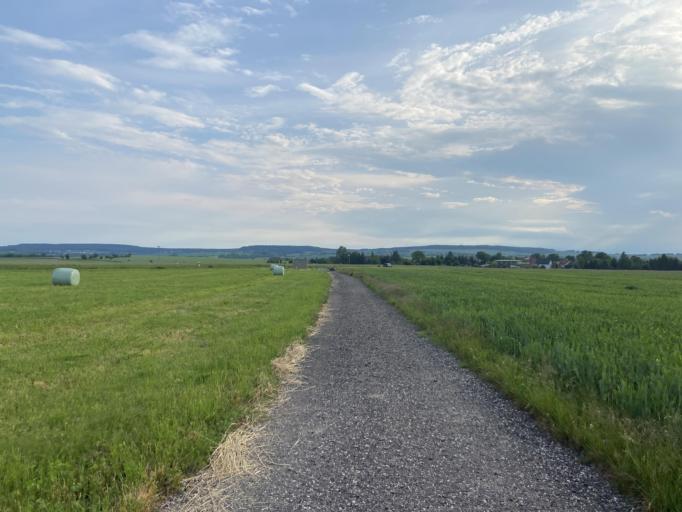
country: DE
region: Saxony
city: Tharandt
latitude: 51.0191
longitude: 13.5841
